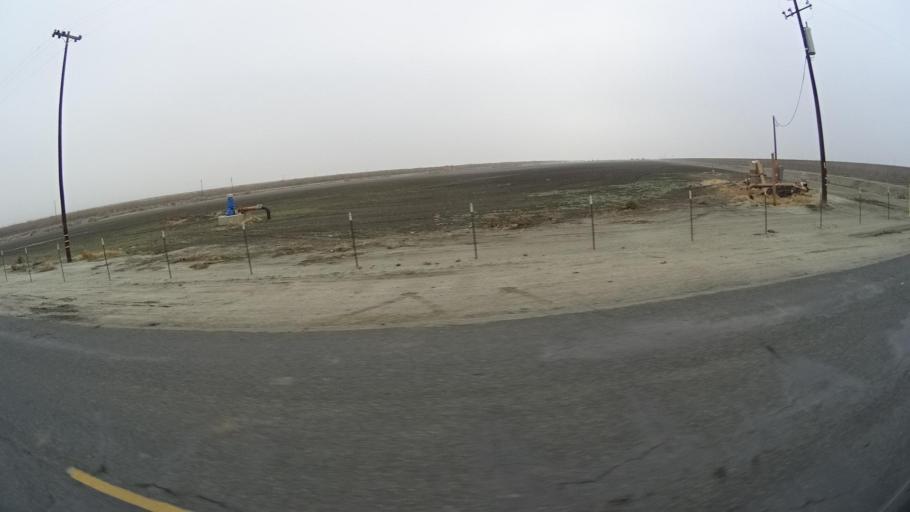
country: US
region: California
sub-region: Kern County
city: Buttonwillow
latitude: 35.3629
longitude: -119.4742
